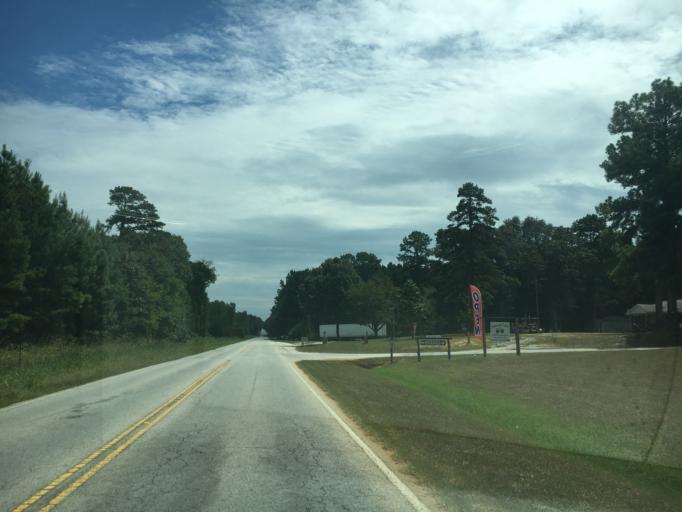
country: US
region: South Carolina
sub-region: Laurens County
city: Laurens
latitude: 34.5677
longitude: -82.0858
